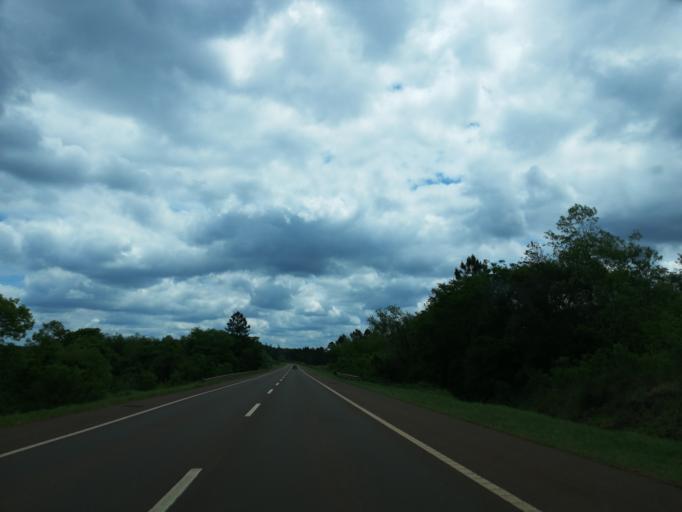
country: AR
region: Misiones
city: Arroyo del Medio
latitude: -27.6419
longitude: -55.3862
